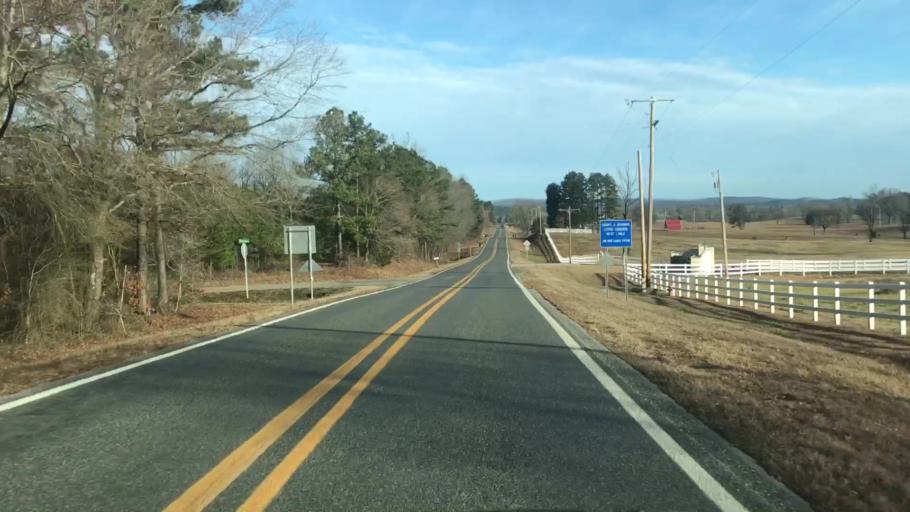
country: US
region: Arkansas
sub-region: Garland County
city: Rockwell
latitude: 34.4952
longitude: -93.2766
